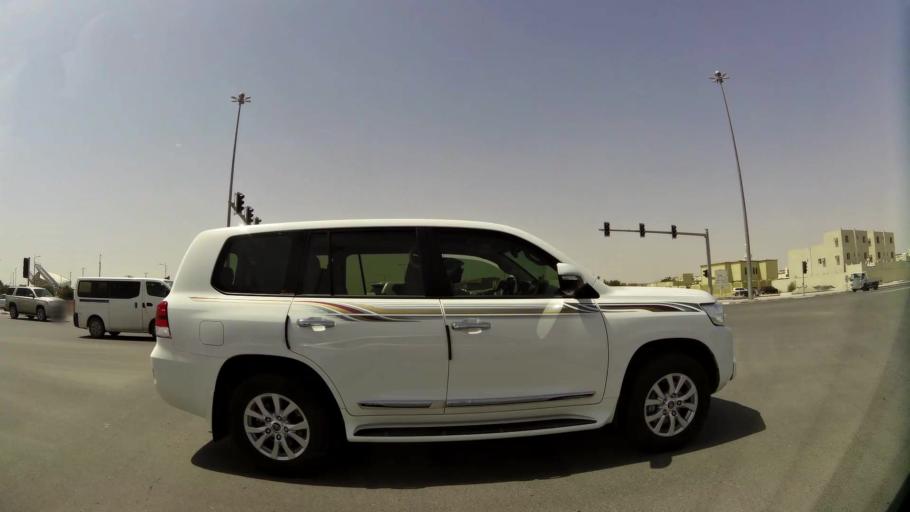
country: QA
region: Baladiyat Umm Salal
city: Umm Salal Muhammad
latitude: 25.3774
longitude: 51.4702
